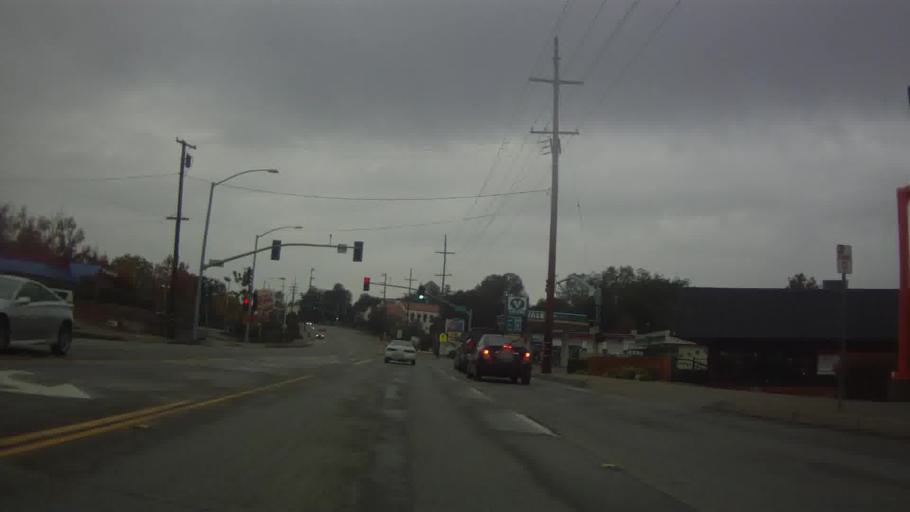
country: US
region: California
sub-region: Shasta County
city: Redding
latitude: 40.5864
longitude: -122.4000
